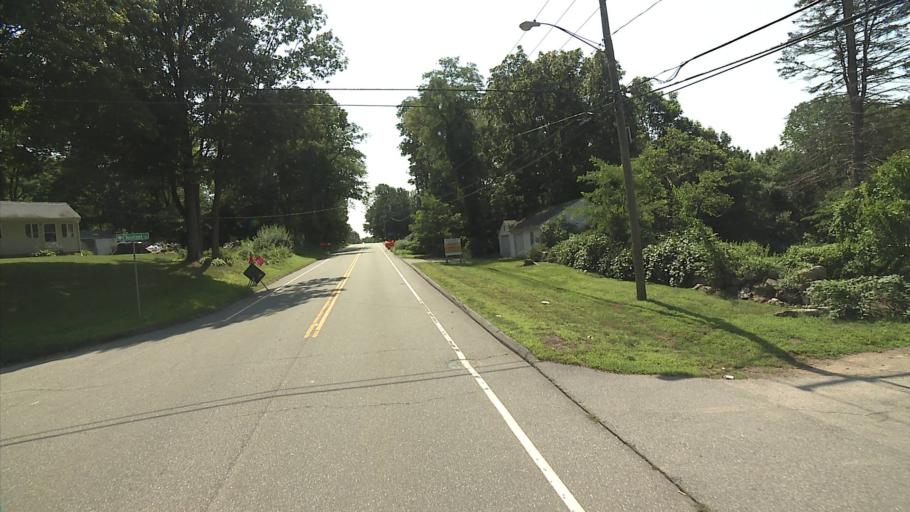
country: US
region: Connecticut
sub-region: New London County
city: Colchester
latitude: 41.5647
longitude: -72.3205
